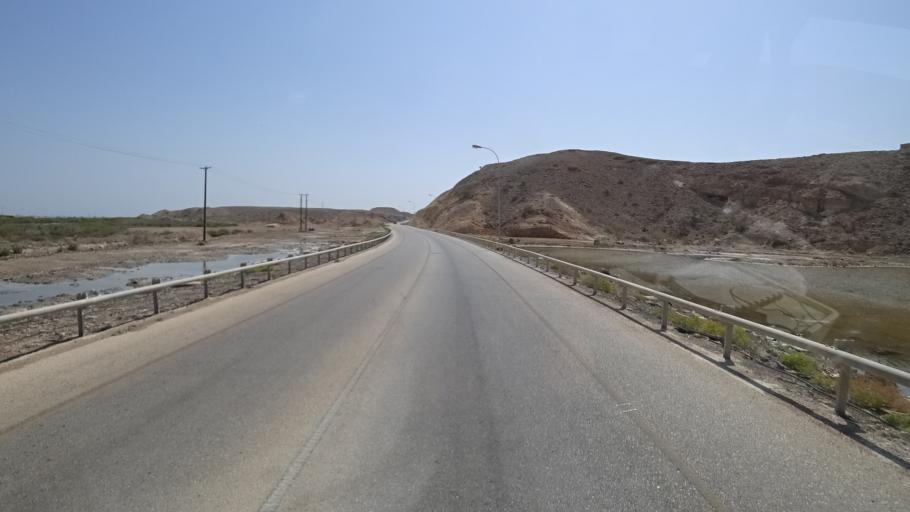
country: OM
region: Ash Sharqiyah
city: Sur
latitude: 22.5423
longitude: 59.5093
